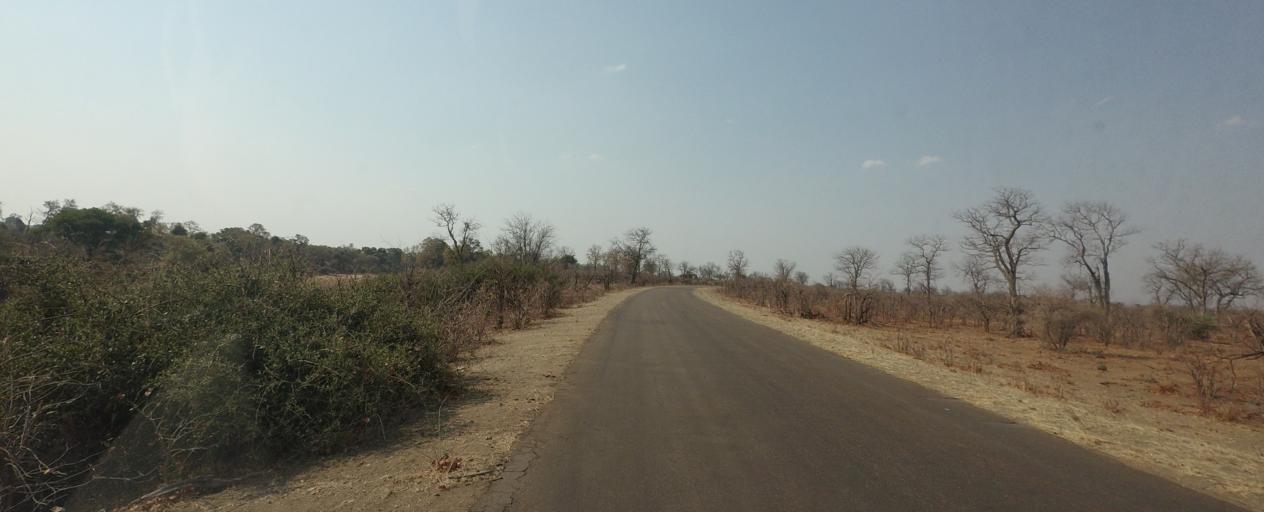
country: ZA
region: Limpopo
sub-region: Mopani District Municipality
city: Giyani
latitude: -23.1033
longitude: 31.3852
